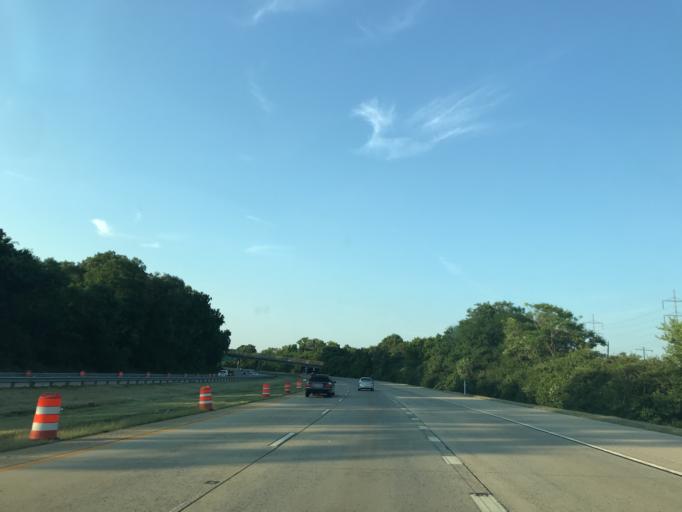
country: US
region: Delaware
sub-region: New Castle County
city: Claymont
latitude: 39.7980
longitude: -75.4527
